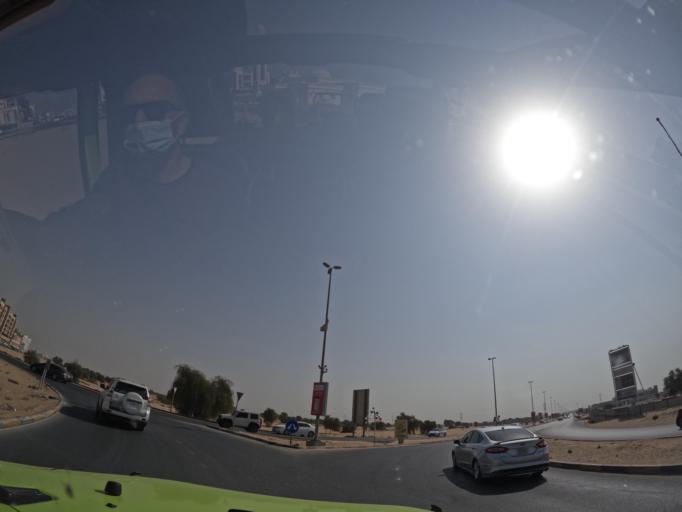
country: AE
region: Ajman
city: Ajman
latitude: 25.3746
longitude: 55.5084
